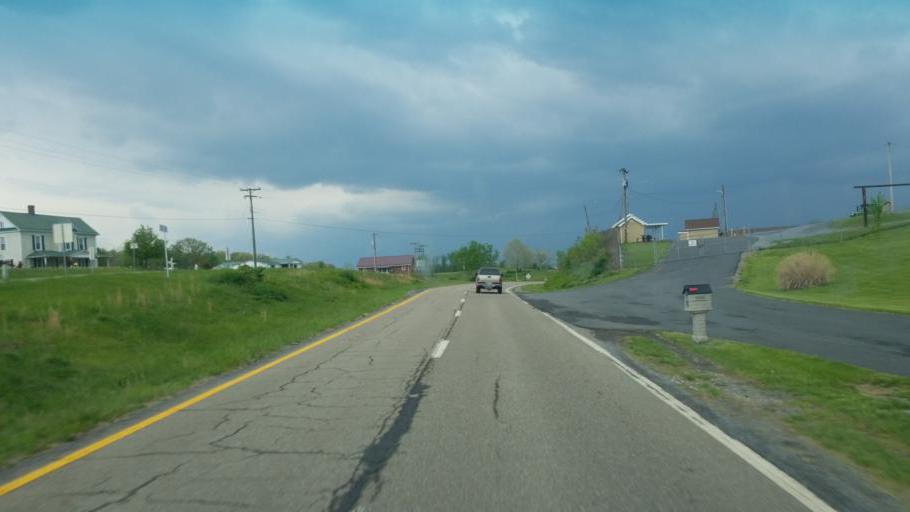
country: US
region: Virginia
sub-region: Washington County
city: Glade Spring
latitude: 36.7750
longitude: -81.7649
